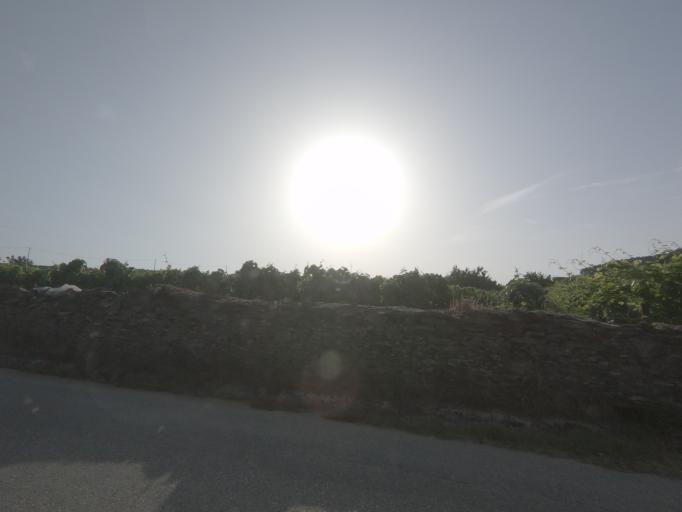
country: PT
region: Vila Real
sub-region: Sabrosa
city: Sabrosa
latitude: 41.2550
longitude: -7.4658
